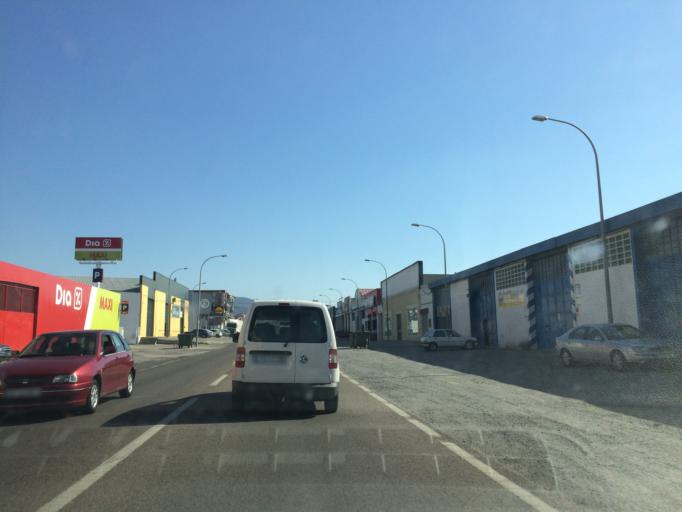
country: ES
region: Extremadura
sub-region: Provincia de Caceres
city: Plasencia
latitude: 40.0207
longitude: -6.0988
